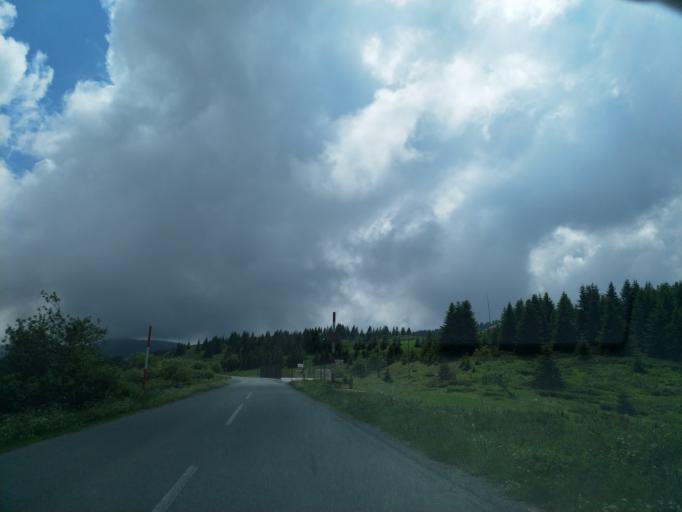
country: XK
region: Mitrovica
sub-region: Komuna e Leposaviqit
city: Leposaviq
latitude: 43.3179
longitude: 20.8367
